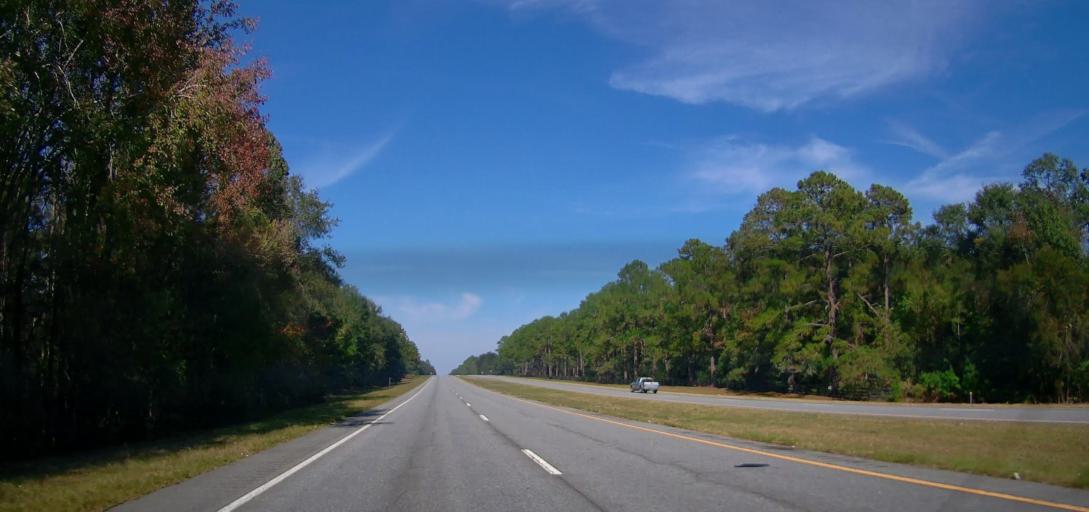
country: US
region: Georgia
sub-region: Lee County
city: Leesburg
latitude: 31.6796
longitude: -83.9948
